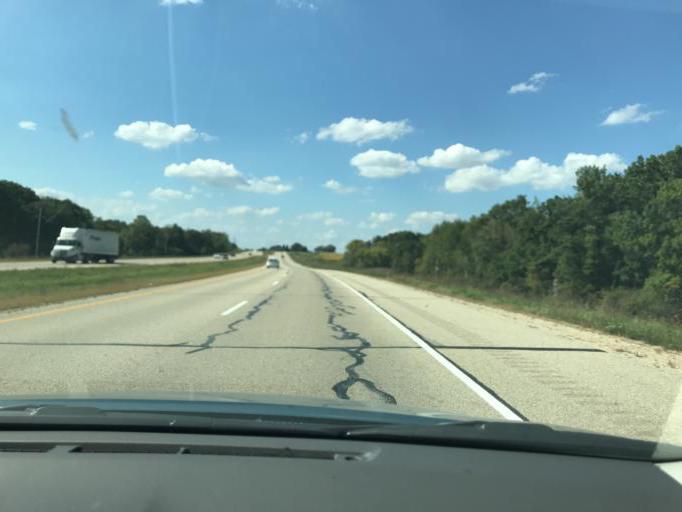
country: US
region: Wisconsin
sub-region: Walworth County
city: Pell Lake
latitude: 42.5903
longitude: -88.3427
